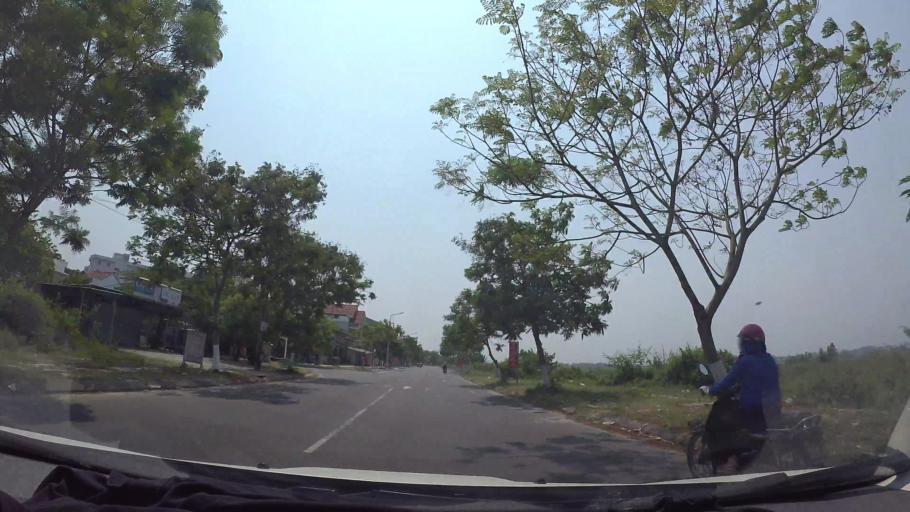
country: VN
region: Da Nang
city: Cam Le
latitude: 16.0030
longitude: 108.2052
